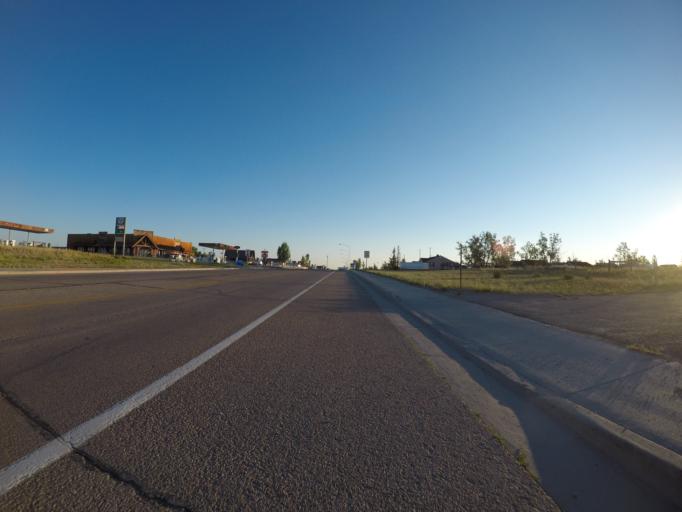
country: US
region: Wyoming
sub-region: Sublette County
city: Marbleton
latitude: 42.5513
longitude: -110.1095
